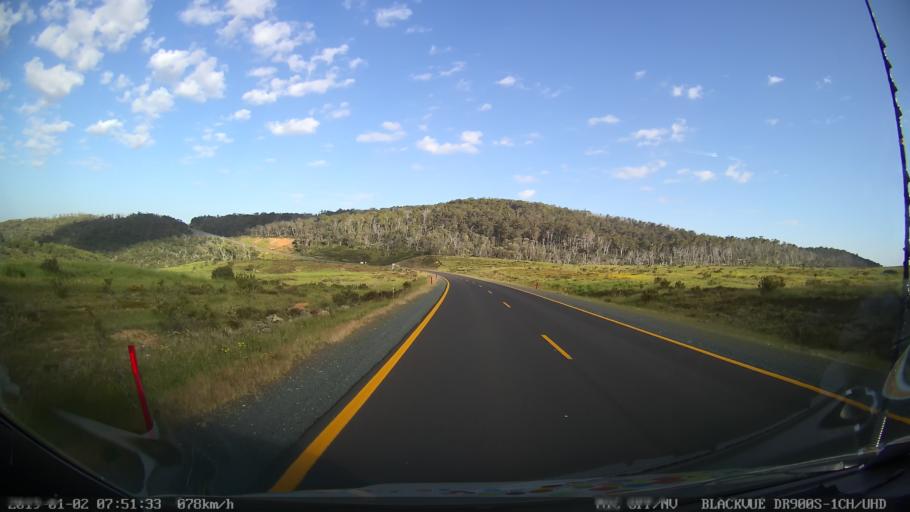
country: AU
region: New South Wales
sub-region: Tumut Shire
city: Tumut
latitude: -35.7172
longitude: 148.5301
